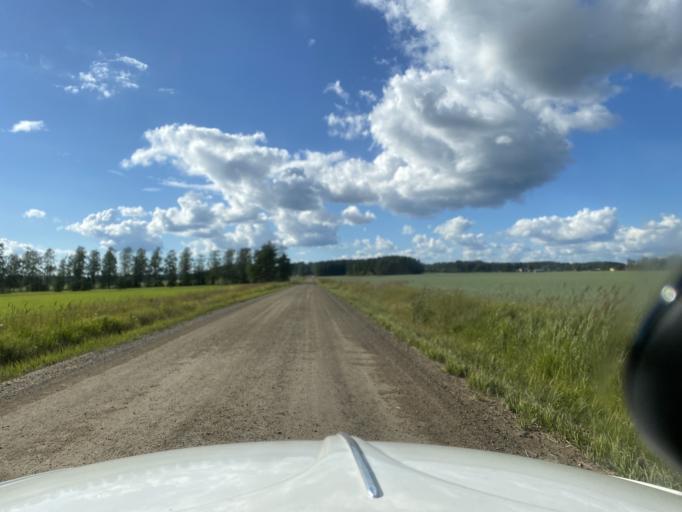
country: FI
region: Pirkanmaa
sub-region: Lounais-Pirkanmaa
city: Punkalaidun
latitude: 61.1337
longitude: 23.2302
